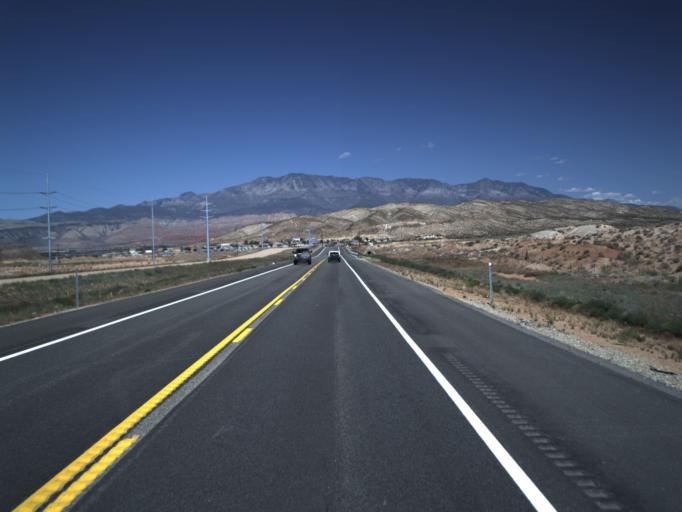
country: US
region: Utah
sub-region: Washington County
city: Washington
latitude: 37.0694
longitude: -113.4859
